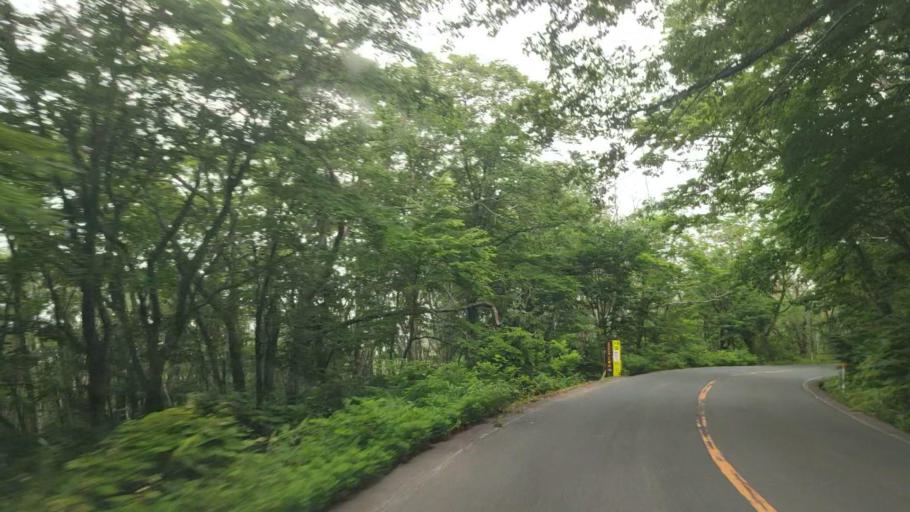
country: JP
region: Tottori
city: Yonago
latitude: 35.3561
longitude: 133.5342
